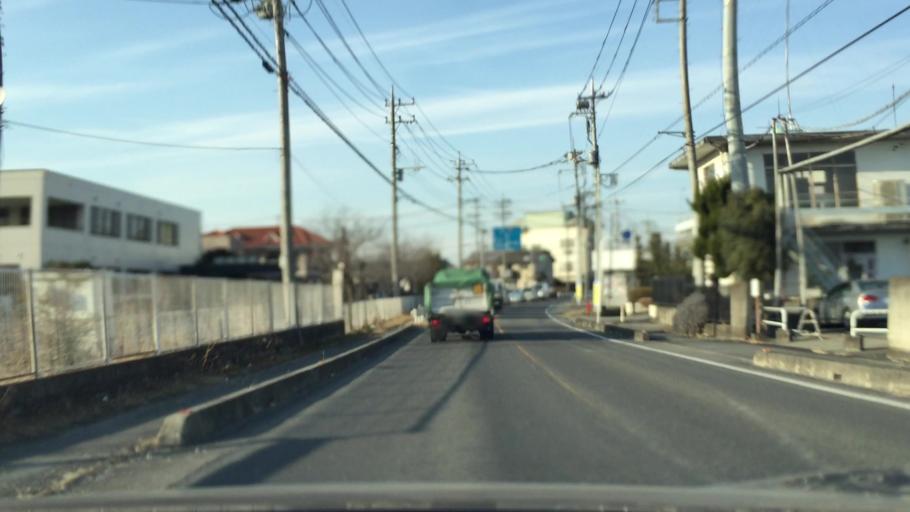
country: JP
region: Saitama
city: Menuma
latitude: 36.2010
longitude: 139.3746
